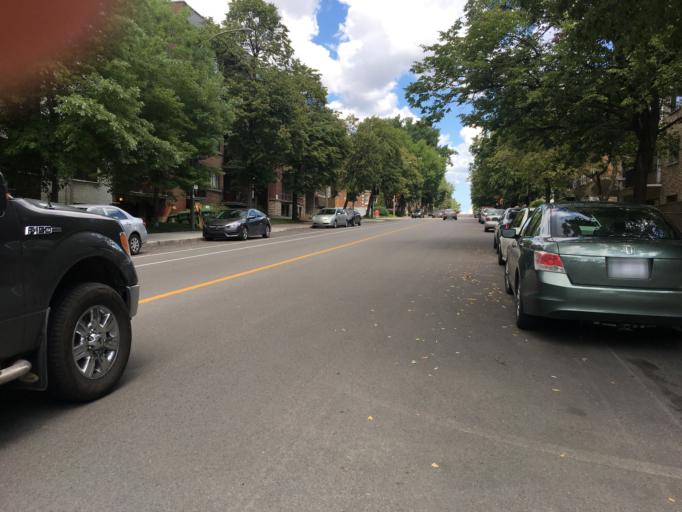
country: CA
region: Quebec
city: Westmount
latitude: 45.4985
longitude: -73.6231
